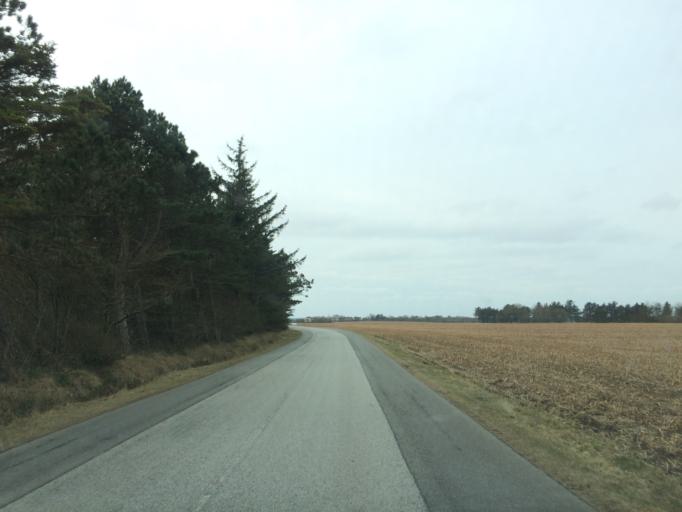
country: DK
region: Central Jutland
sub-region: Ringkobing-Skjern Kommune
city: Tarm
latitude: 55.8017
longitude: 8.3804
